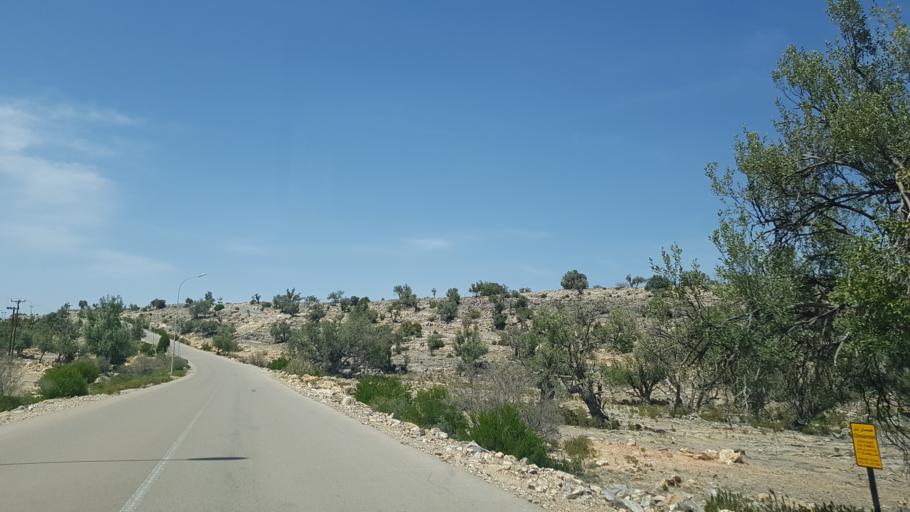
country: OM
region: Al Batinah
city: Bayt al `Awabi
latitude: 23.1214
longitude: 57.6028
